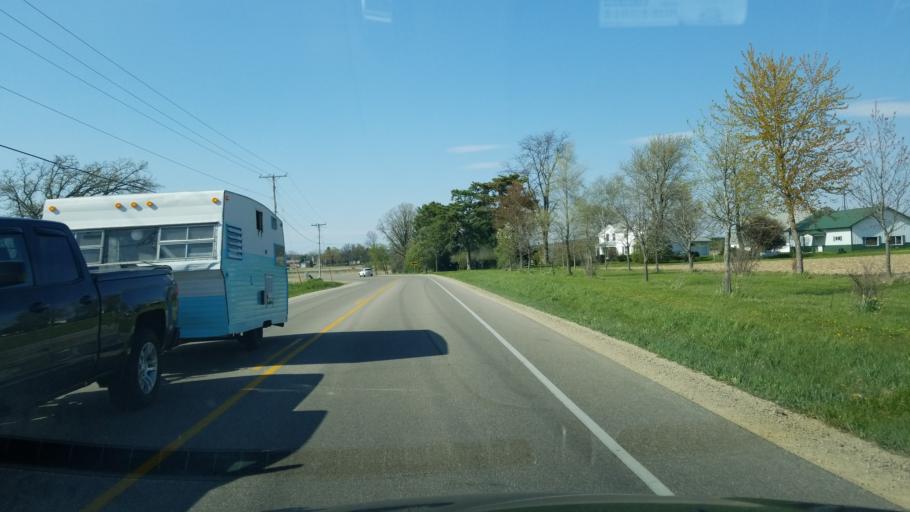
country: US
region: Wisconsin
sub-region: Dane County
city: Fitchburg
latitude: 42.9392
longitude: -89.4374
